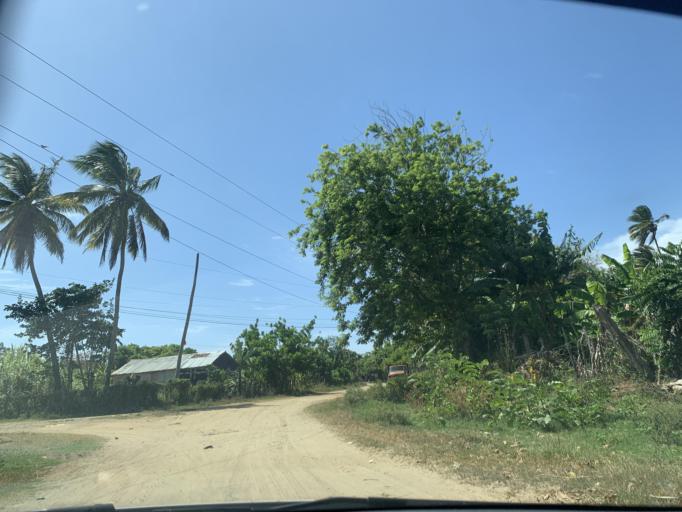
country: DO
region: Puerto Plata
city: Luperon
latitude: 19.8883
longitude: -70.8760
